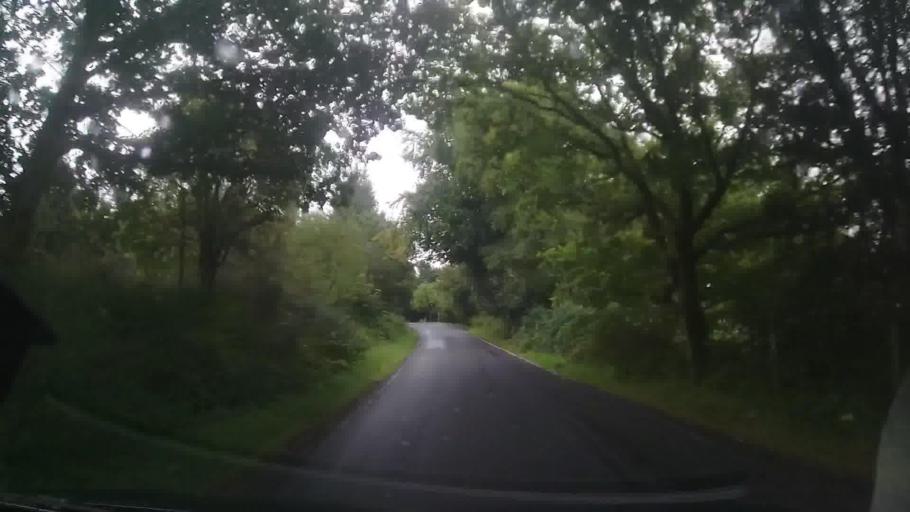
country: GB
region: Scotland
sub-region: Argyll and Bute
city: Oban
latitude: 56.6920
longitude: -5.5935
